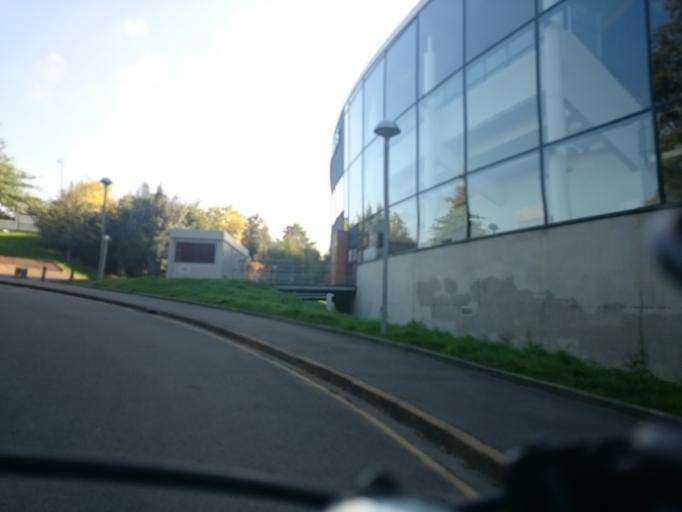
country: FR
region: Brittany
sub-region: Departement d'Ille-et-Vilaine
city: Cesson-Sevigne
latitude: 48.1153
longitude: -1.5963
